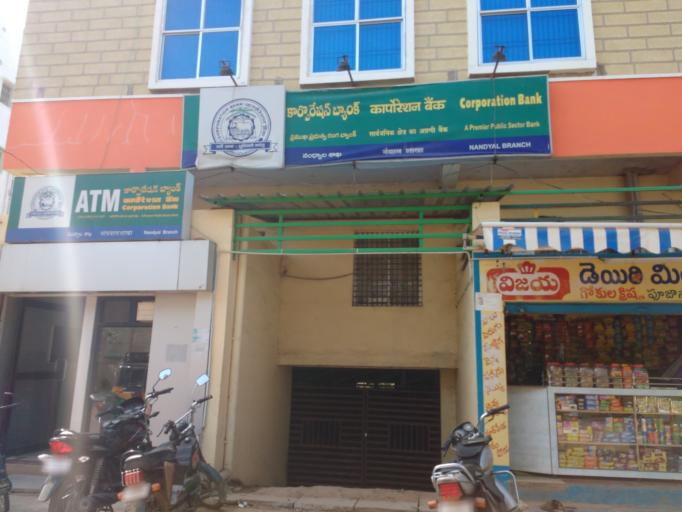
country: IN
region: Andhra Pradesh
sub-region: Kurnool
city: Nandyal
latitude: 15.4842
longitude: 78.4813
